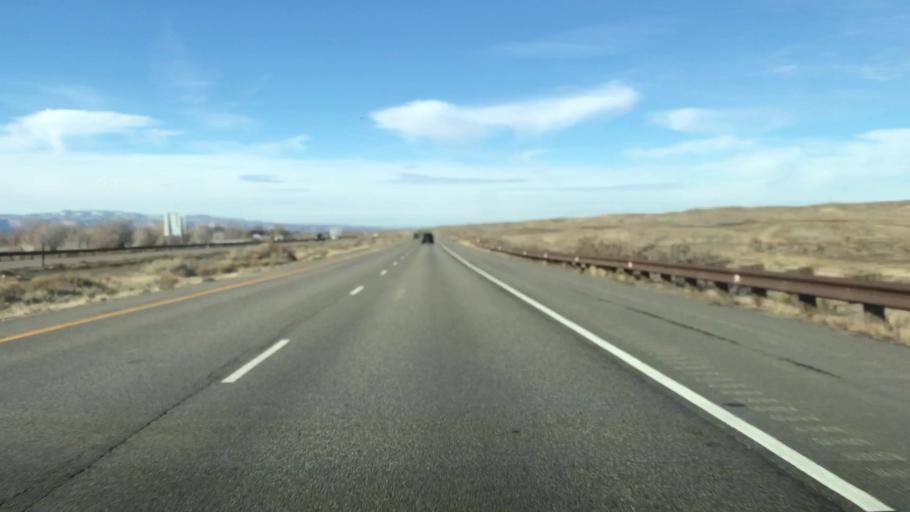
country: US
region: Colorado
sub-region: Mesa County
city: Clifton
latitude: 39.1040
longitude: -108.4654
